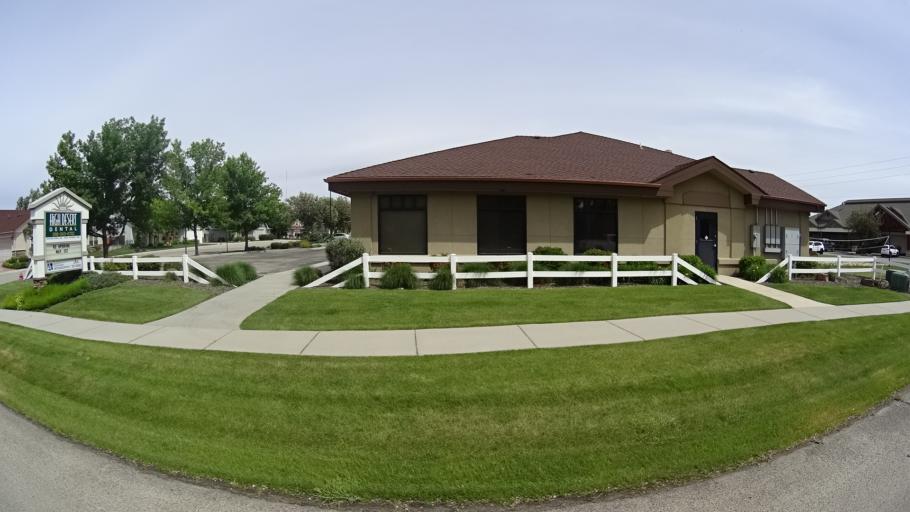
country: US
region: Idaho
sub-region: Ada County
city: Meridian
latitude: 43.5612
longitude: -116.3355
